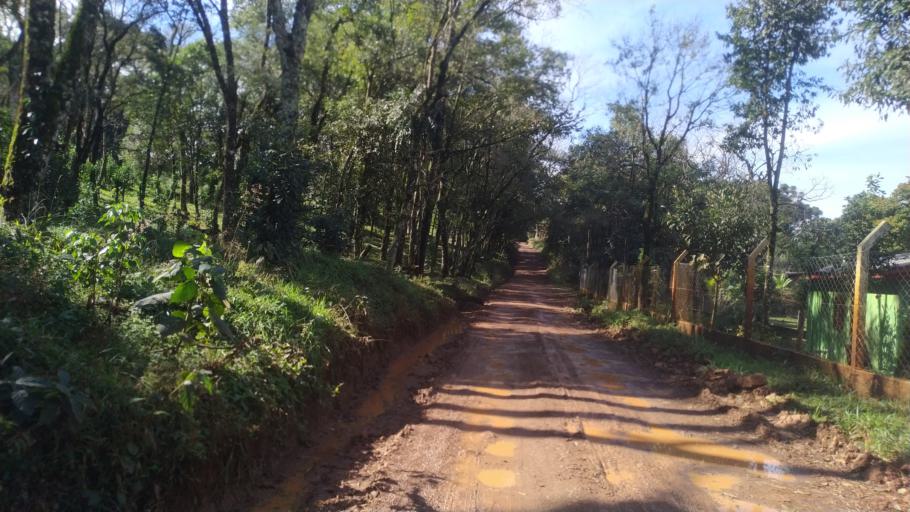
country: BR
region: Santa Catarina
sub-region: Chapeco
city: Chapeco
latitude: -27.1619
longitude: -52.6029
